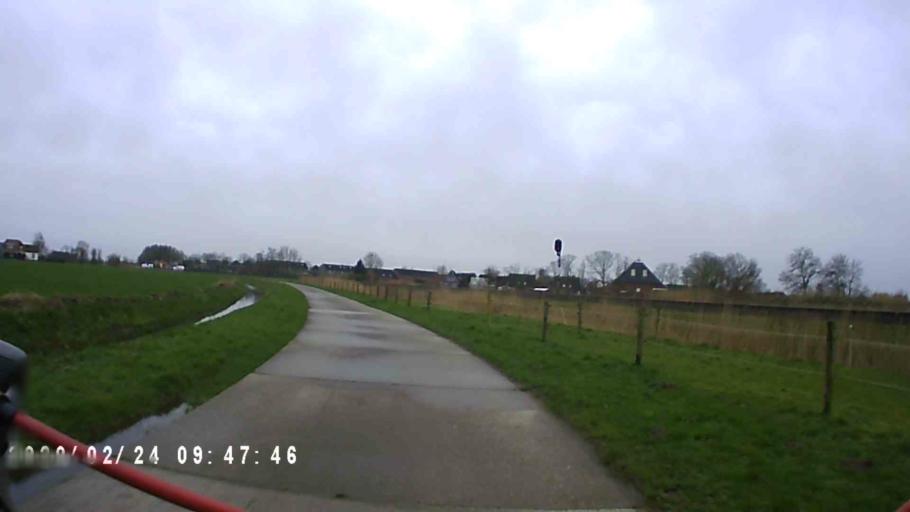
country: NL
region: Groningen
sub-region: Gemeente Winsum
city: Winsum
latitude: 53.2947
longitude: 6.5419
